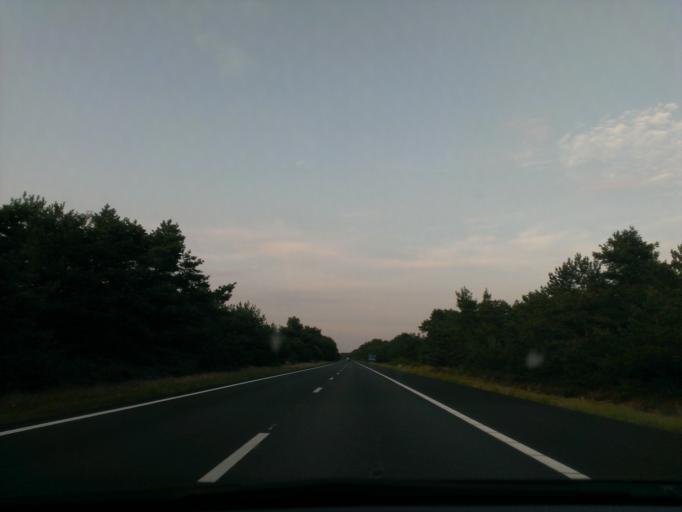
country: NL
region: Gelderland
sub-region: Gemeente Nunspeet
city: Nunspeet
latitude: 52.3872
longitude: 5.8409
